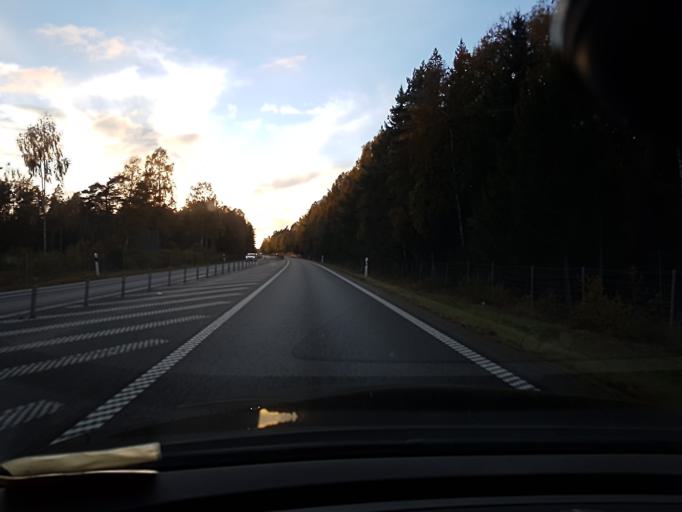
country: SE
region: Kronoberg
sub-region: Ljungby Kommun
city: Ljungby
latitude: 56.8519
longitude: 14.0040
